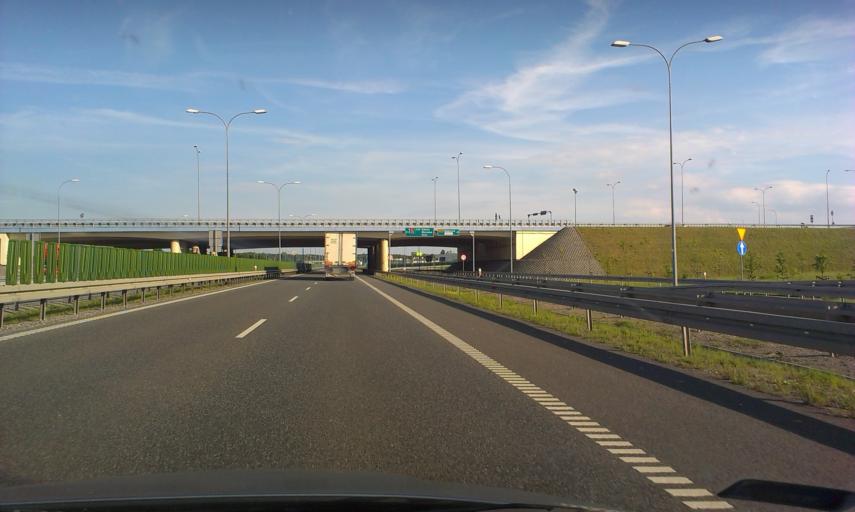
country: PL
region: Kujawsko-Pomorskie
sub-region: Powiat bydgoski
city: Biale Blota
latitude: 53.0958
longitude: 17.8956
